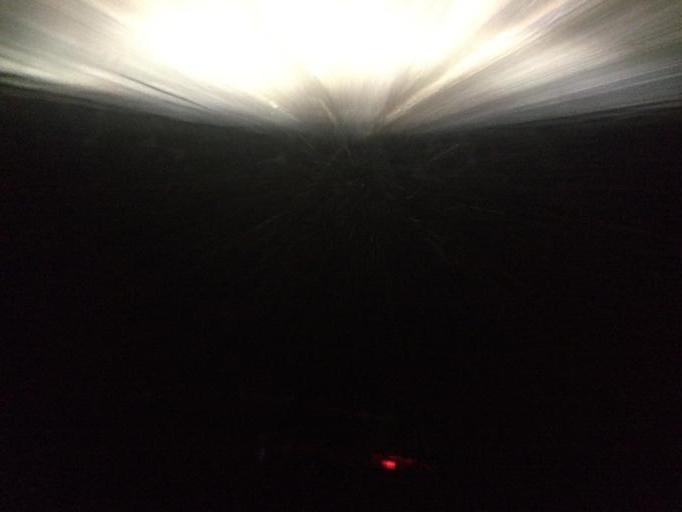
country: RU
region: Tula
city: Dubna
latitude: 54.0654
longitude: 37.0398
